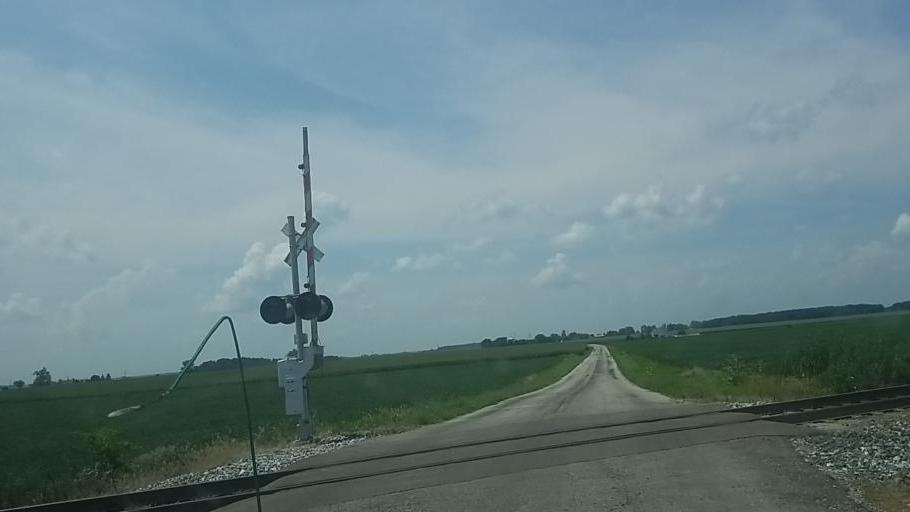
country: US
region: Ohio
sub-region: Marion County
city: Marion
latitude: 40.6736
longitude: -83.2026
